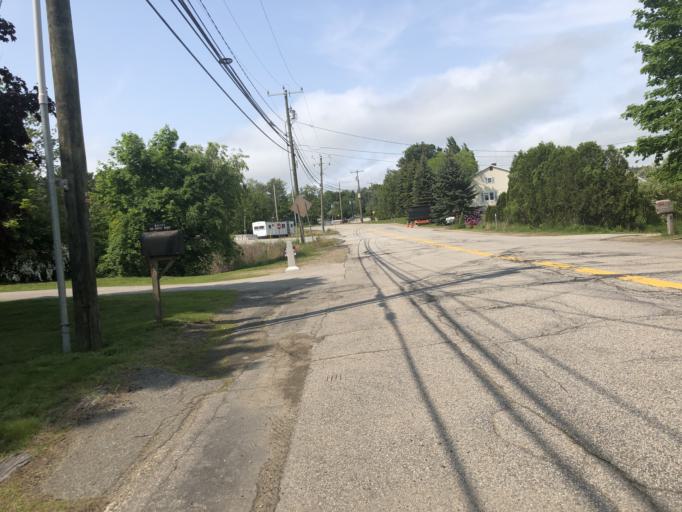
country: US
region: Maine
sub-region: York County
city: Eliot
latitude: 43.1317
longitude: -70.8360
